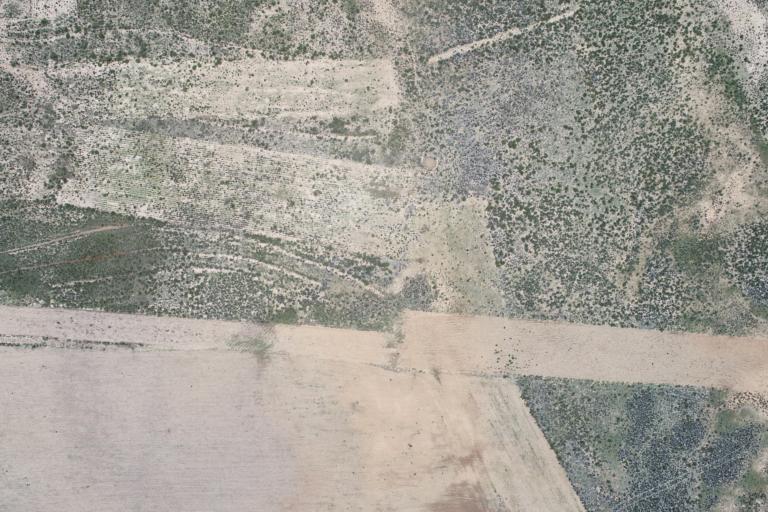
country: BO
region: La Paz
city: Patacamaya
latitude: -17.2841
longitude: -68.5008
